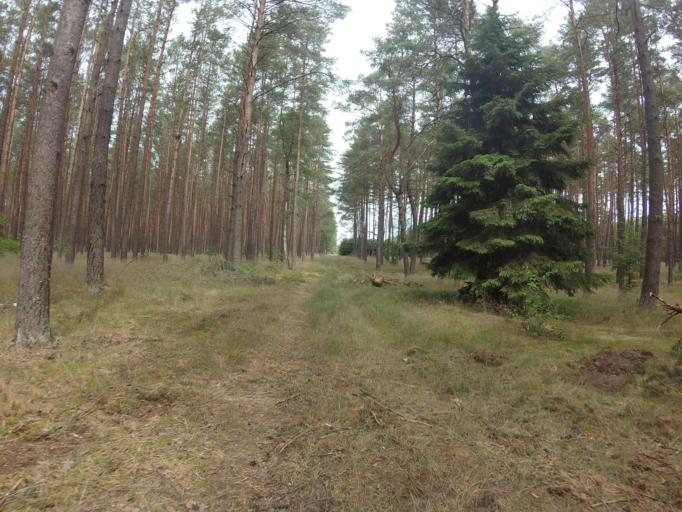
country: PL
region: West Pomeranian Voivodeship
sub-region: Powiat choszczenski
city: Bierzwnik
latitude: 53.1097
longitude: 15.6754
